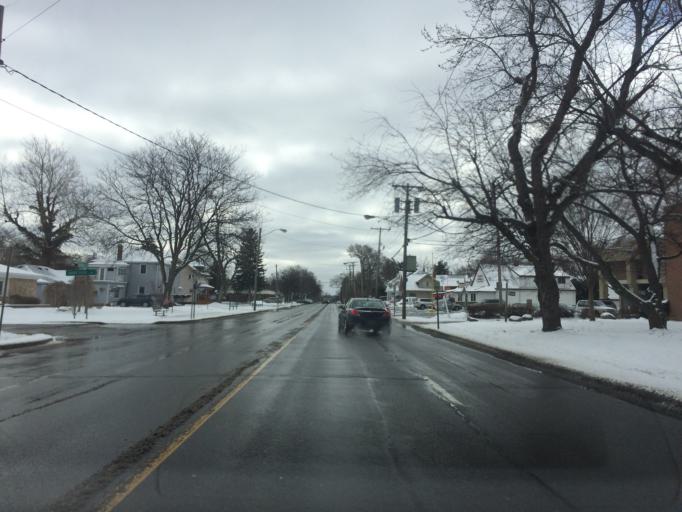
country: US
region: New York
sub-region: Monroe County
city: Brighton
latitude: 43.1231
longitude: -77.5609
